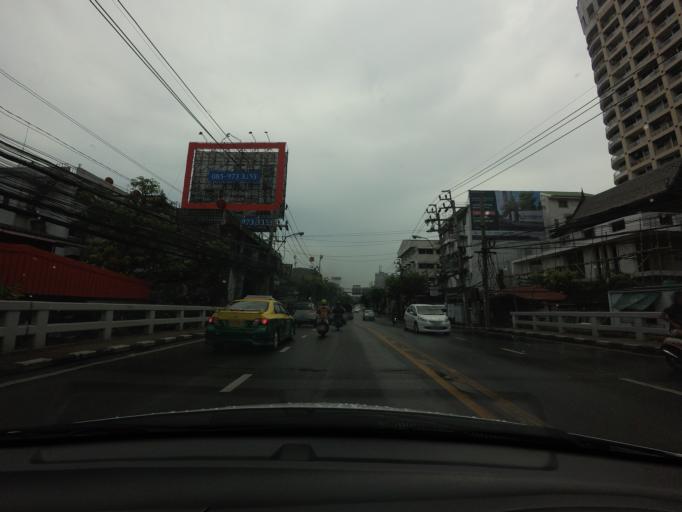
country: TH
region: Bangkok
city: Suan Luang
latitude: 13.7119
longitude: 100.6409
